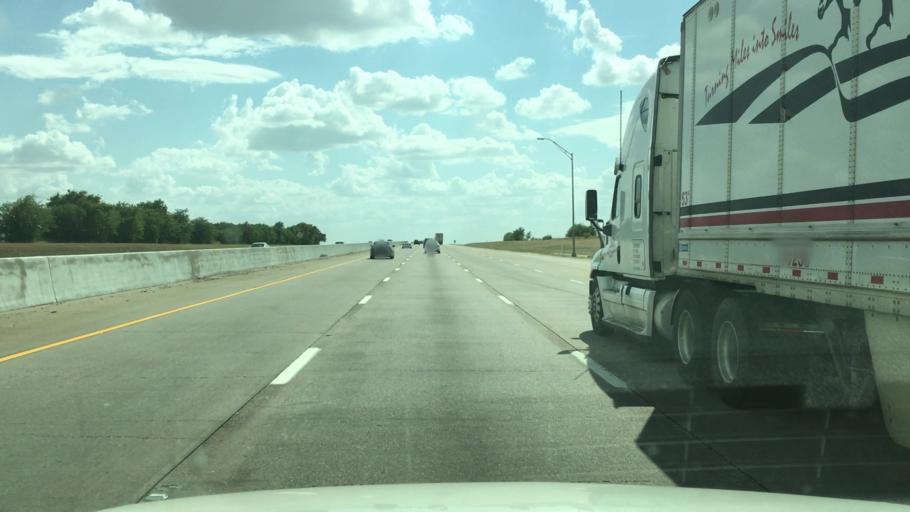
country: US
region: Texas
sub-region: Ellis County
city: Plum Grove
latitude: 32.1312
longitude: -96.9606
